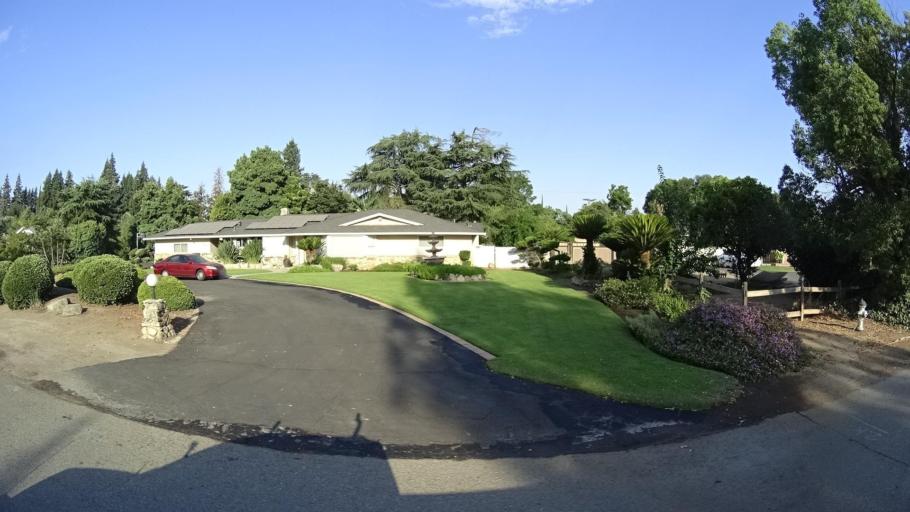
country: US
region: California
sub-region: Fresno County
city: Sunnyside
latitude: 36.7253
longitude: -119.7000
